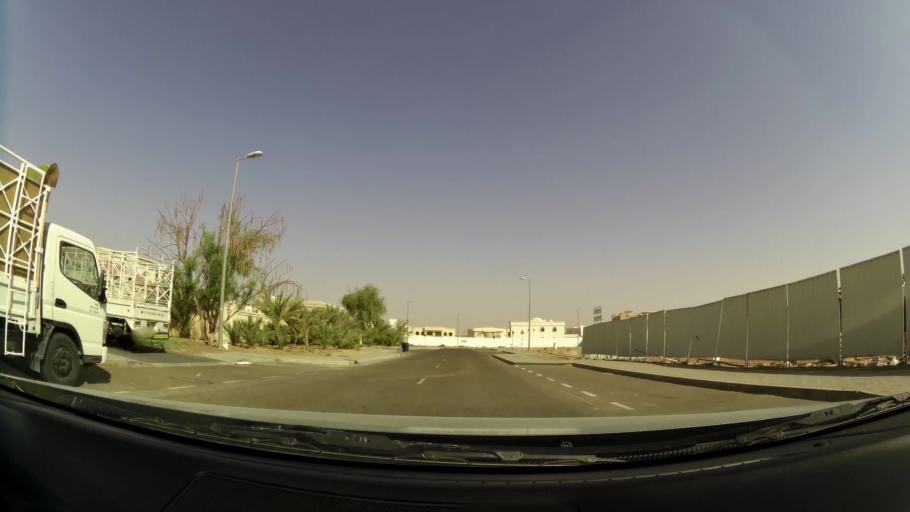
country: OM
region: Al Buraimi
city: Al Buraymi
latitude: 24.3500
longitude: 55.7881
